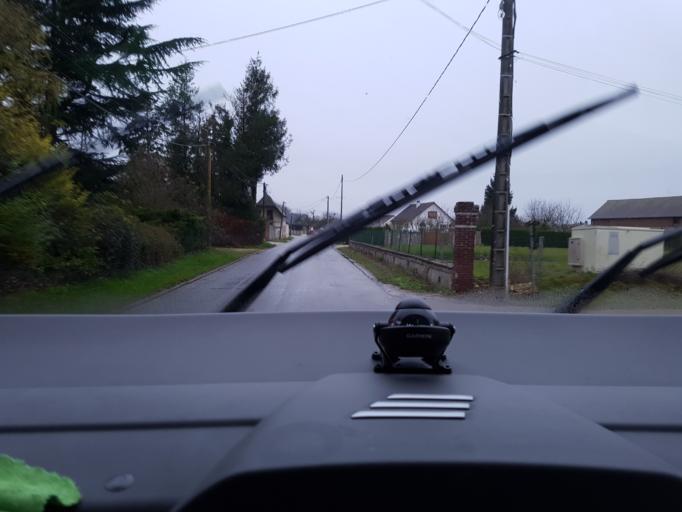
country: FR
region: Haute-Normandie
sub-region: Departement de l'Eure
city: Le Neubourg
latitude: 49.1900
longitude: 0.9491
